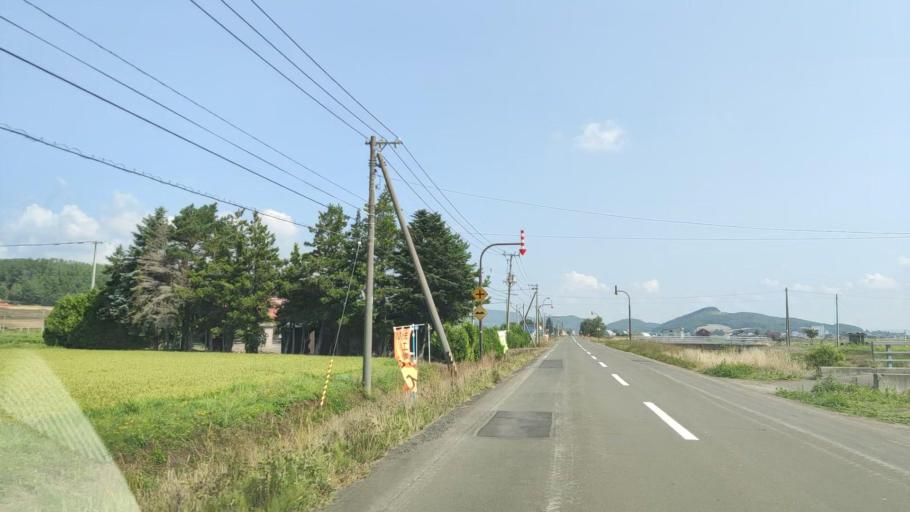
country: JP
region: Hokkaido
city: Shimo-furano
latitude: 43.3754
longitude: 142.3893
